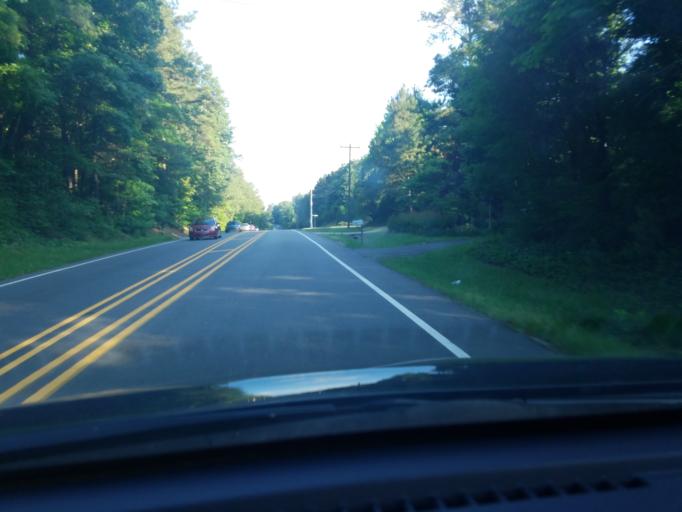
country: US
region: North Carolina
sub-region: Durham County
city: Durham
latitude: 35.9427
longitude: -78.9663
